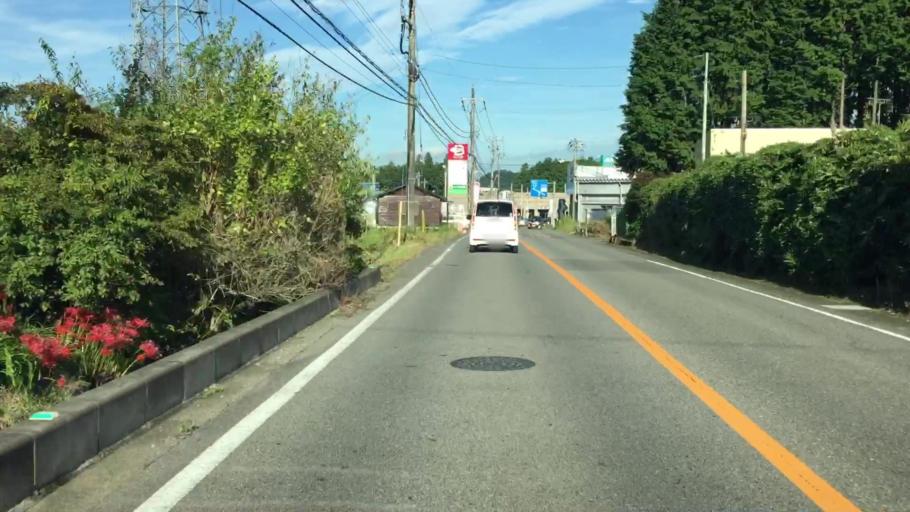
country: JP
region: Tochigi
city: Imaichi
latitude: 36.7379
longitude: 139.7067
